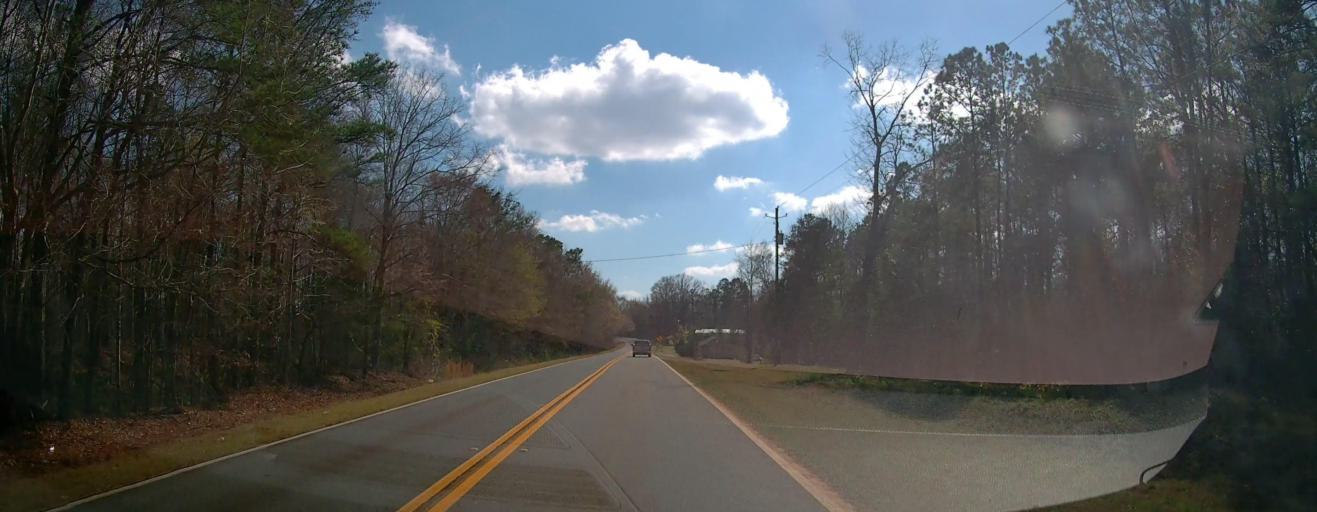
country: US
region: Georgia
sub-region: Twiggs County
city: Jeffersonville
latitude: 32.7114
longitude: -83.3490
